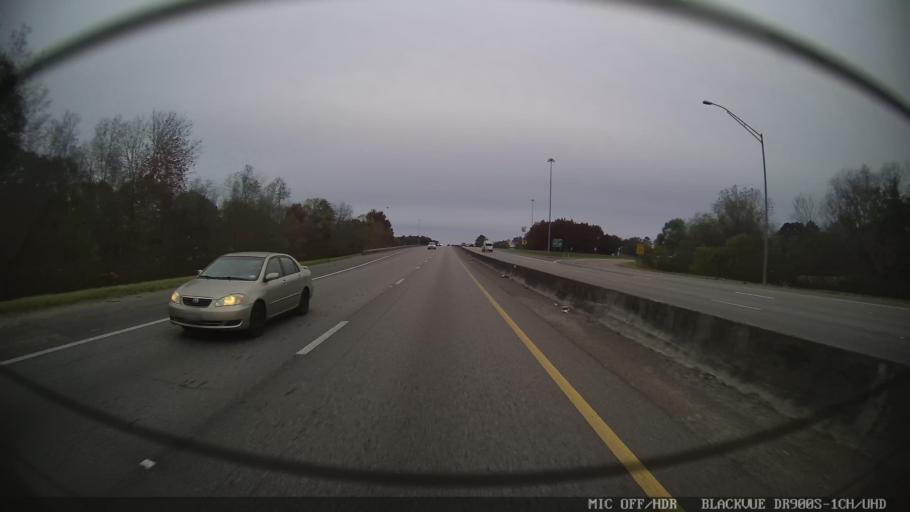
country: US
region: Mississippi
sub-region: Jones County
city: Laurel
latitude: 31.7005
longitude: -89.1191
